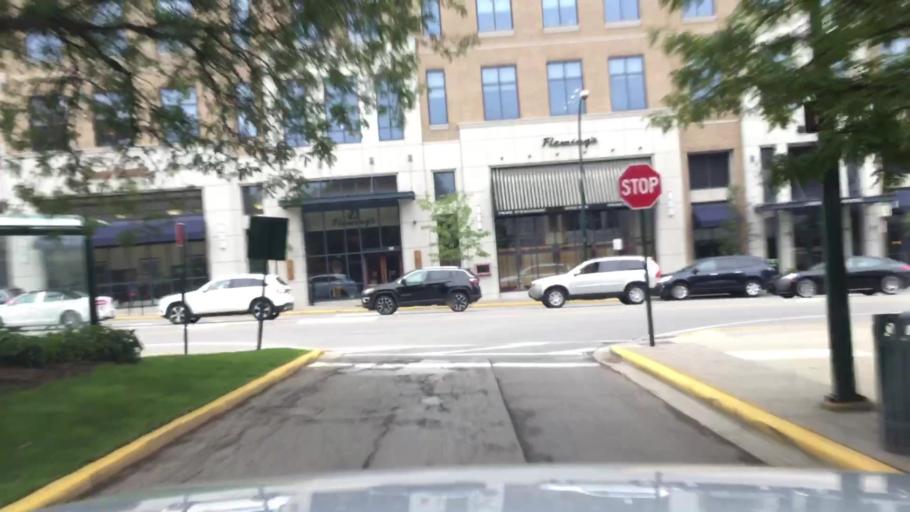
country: US
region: Michigan
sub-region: Oakland County
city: Birmingham
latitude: 42.5482
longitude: -83.2153
